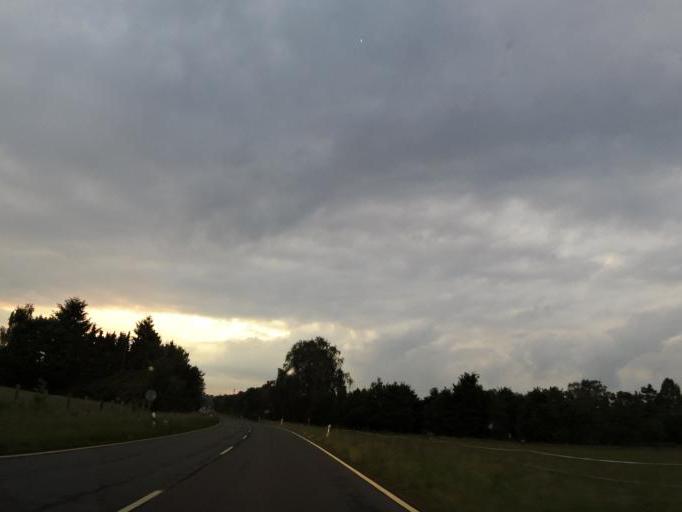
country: DE
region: Hesse
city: Dieburg
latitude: 49.9038
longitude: 8.8160
